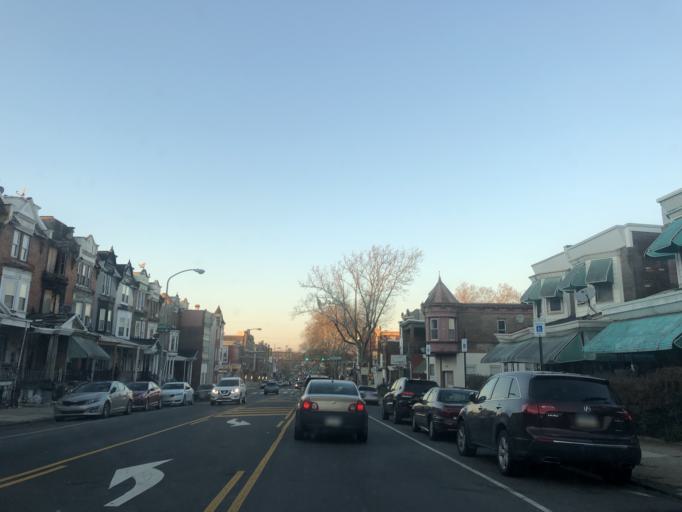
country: US
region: Pennsylvania
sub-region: Delaware County
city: Millbourne
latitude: 39.9673
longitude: -75.2251
